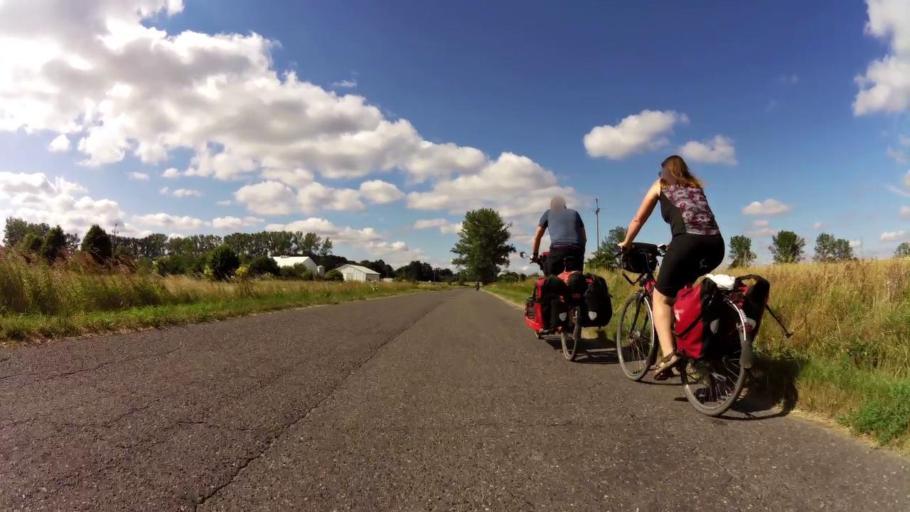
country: PL
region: West Pomeranian Voivodeship
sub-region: Powiat lobeski
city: Lobez
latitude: 53.6355
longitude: 15.6755
